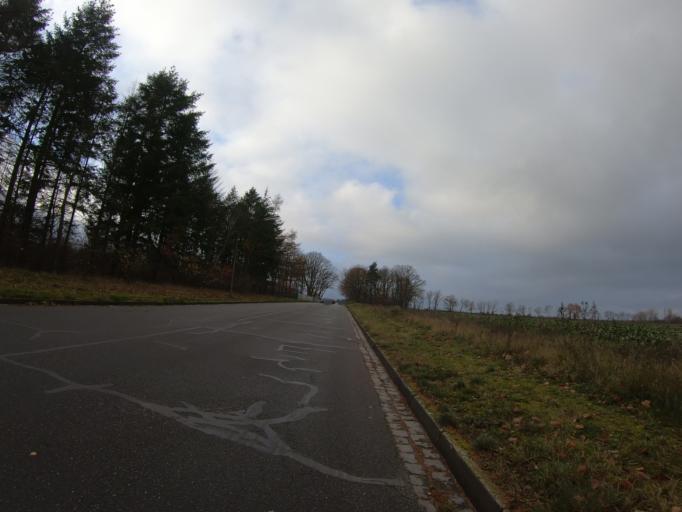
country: DE
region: Lower Saxony
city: Wesendorf
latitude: 52.5838
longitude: 10.5267
